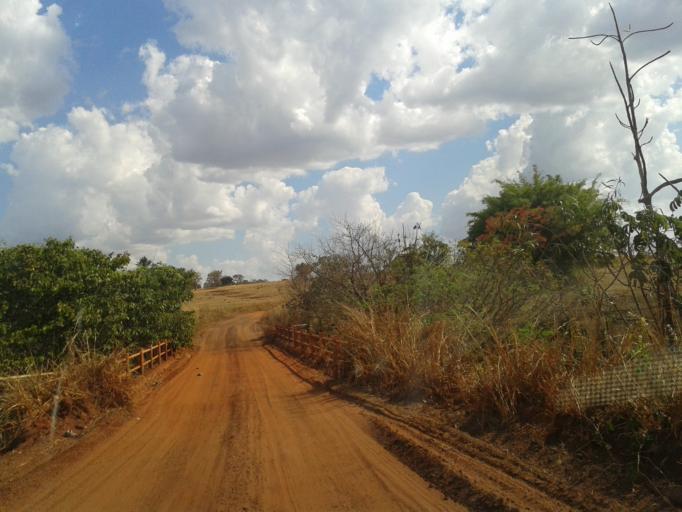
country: BR
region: Minas Gerais
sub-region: Santa Vitoria
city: Santa Vitoria
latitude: -19.2025
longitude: -49.8945
